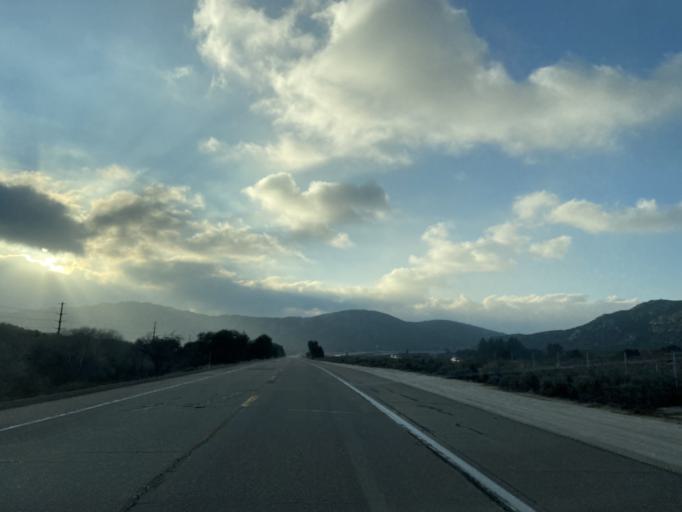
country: US
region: California
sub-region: San Diego County
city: Campo
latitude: 32.7182
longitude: -116.4583
